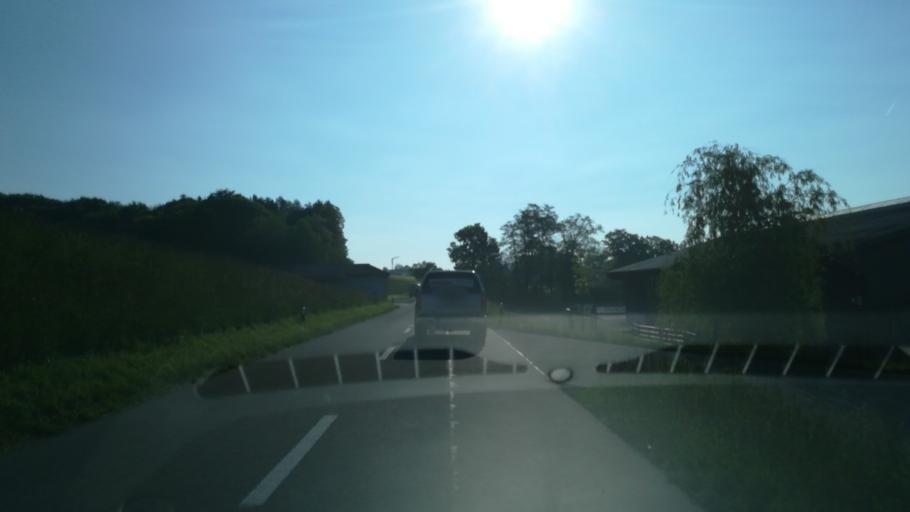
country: CH
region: Thurgau
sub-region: Frauenfeld District
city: Homburg
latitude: 47.6348
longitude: 9.0157
